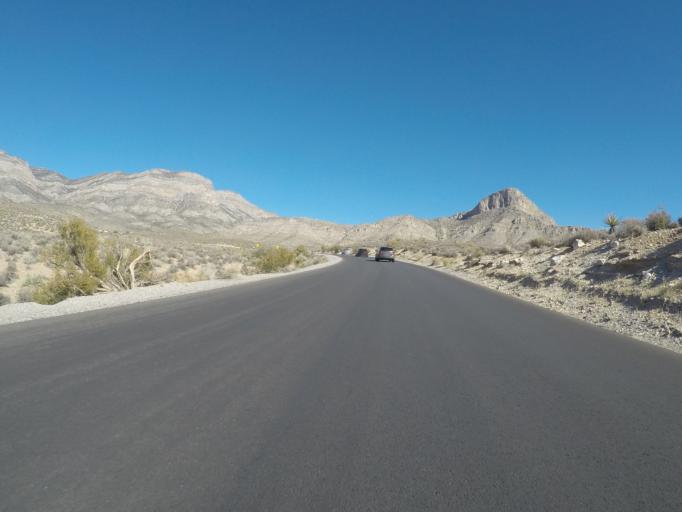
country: US
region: Nevada
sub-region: Clark County
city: Summerlin South
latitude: 36.1668
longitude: -115.4619
